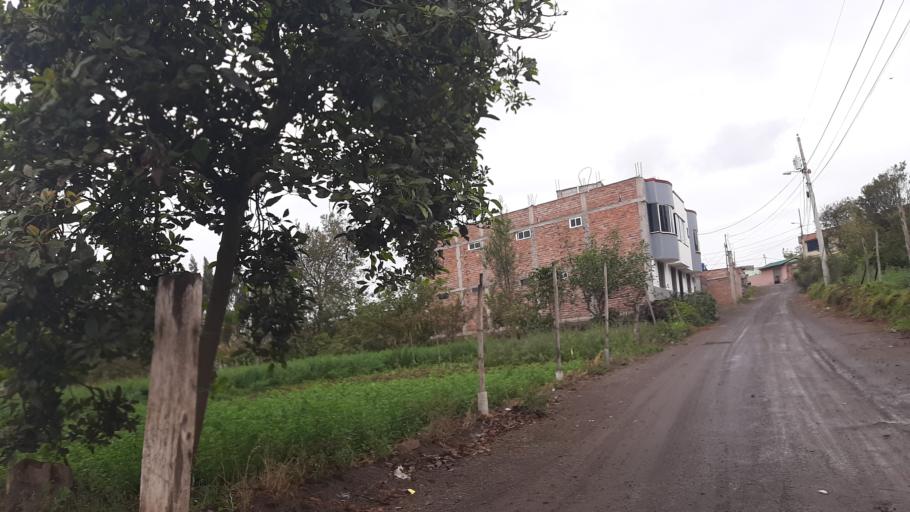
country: EC
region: Chimborazo
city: Riobamba
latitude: -1.6506
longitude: -78.6371
